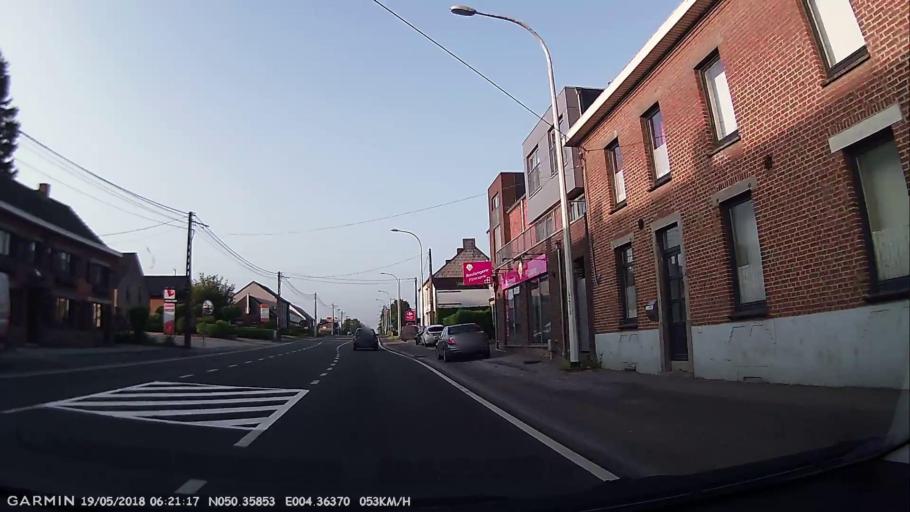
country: BE
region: Wallonia
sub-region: Province du Hainaut
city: Thuin
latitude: 50.3585
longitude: 4.3637
